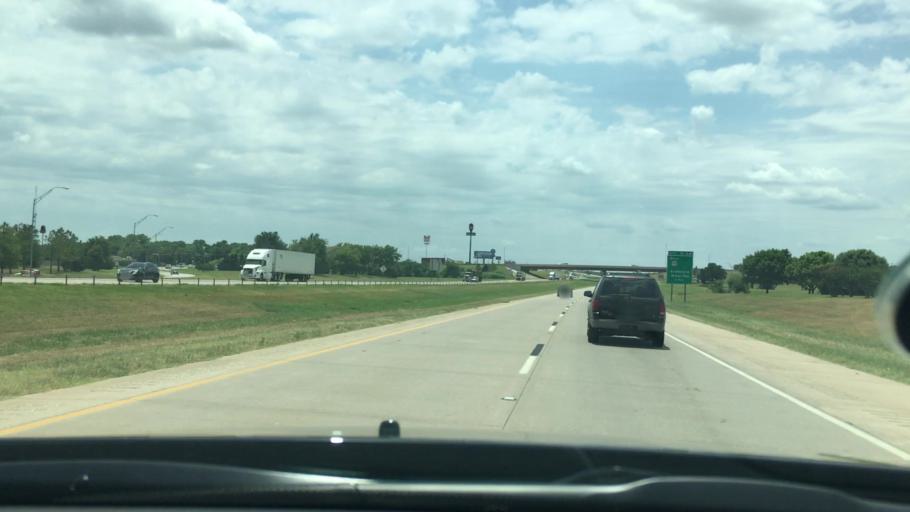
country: US
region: Oklahoma
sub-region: Carter County
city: Ardmore
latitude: 34.1918
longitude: -97.1650
